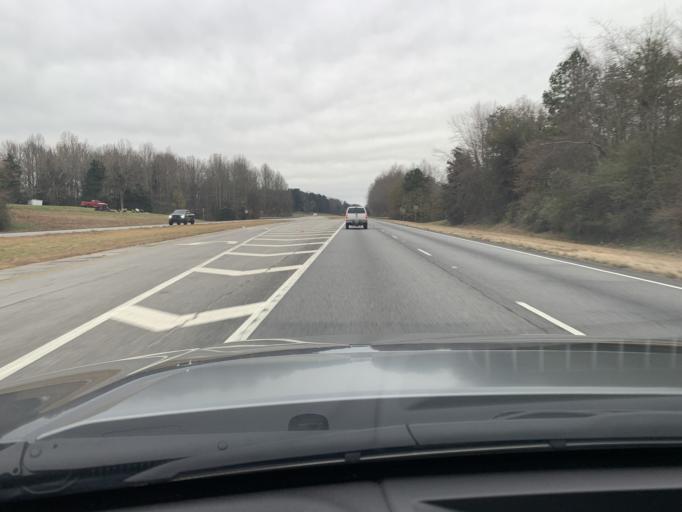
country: US
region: Georgia
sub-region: Habersham County
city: Raoul
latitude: 34.4416
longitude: -83.6271
